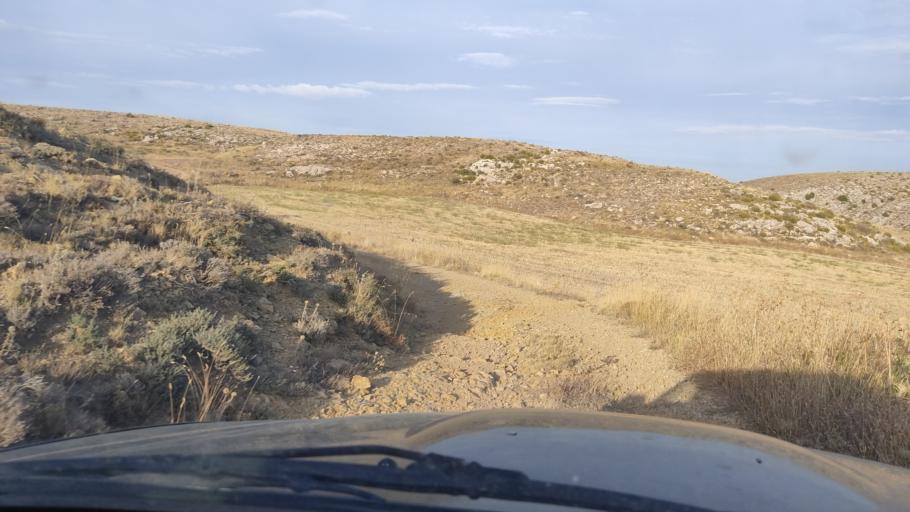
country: ES
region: Aragon
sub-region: Provincia de Teruel
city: Monforte de Moyuela
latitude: 41.0568
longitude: -0.9745
